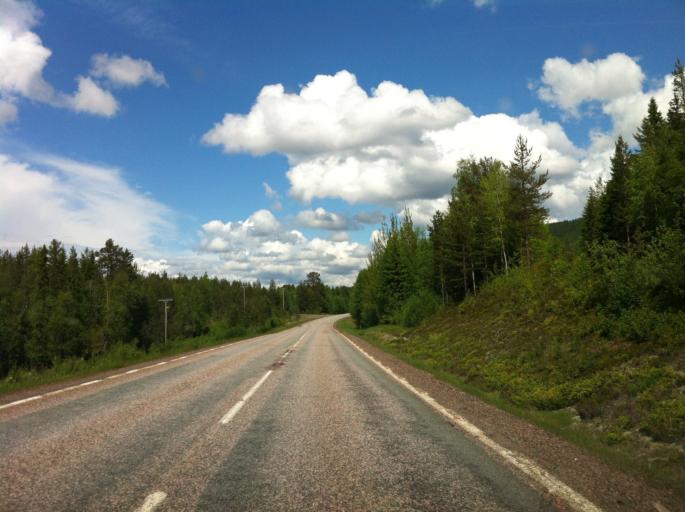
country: SE
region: Dalarna
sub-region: Malung-Saelens kommun
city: Malung
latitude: 61.0083
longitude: 13.3311
